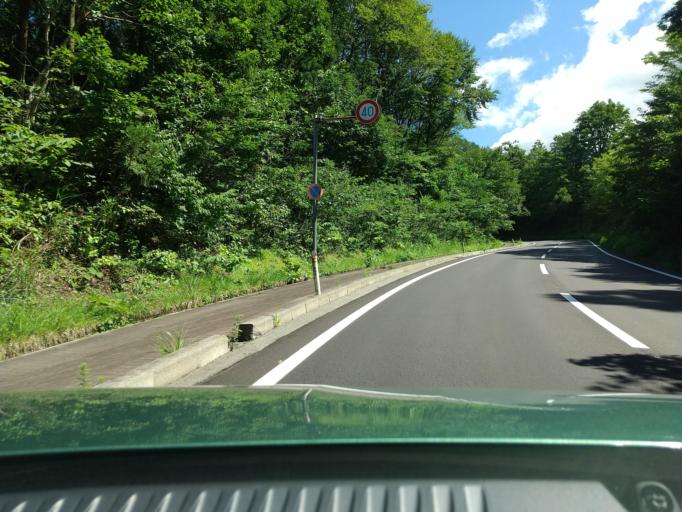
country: JP
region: Iwate
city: Shizukuishi
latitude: 39.7656
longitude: 140.7539
